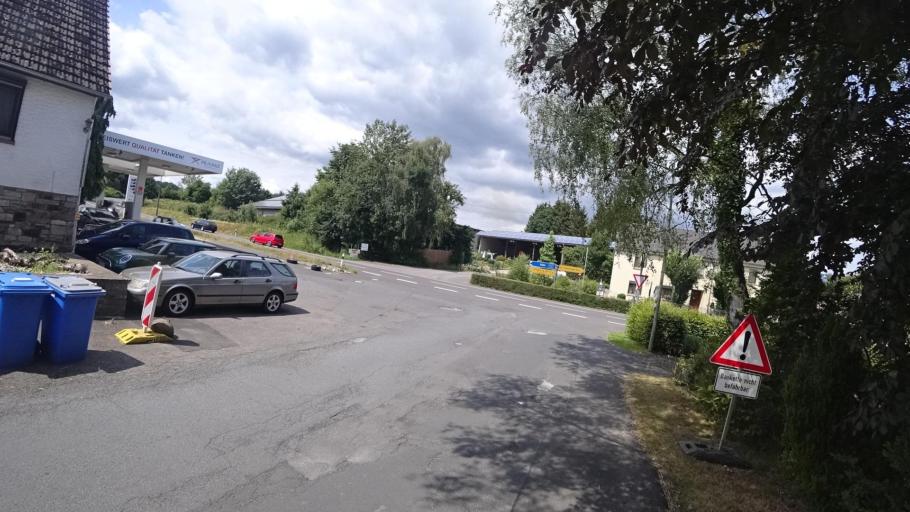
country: DE
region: Rheinland-Pfalz
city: Forstmehren
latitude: 50.7103
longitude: 7.5323
